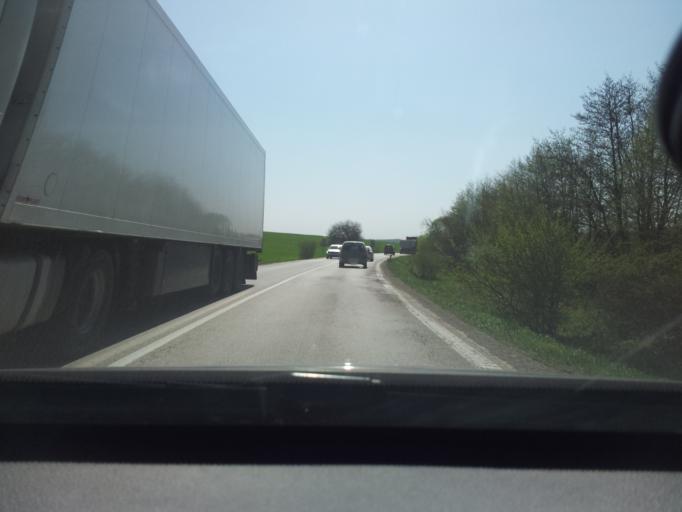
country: SK
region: Nitriansky
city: Trencianske Teplice
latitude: 48.8020
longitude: 18.1277
